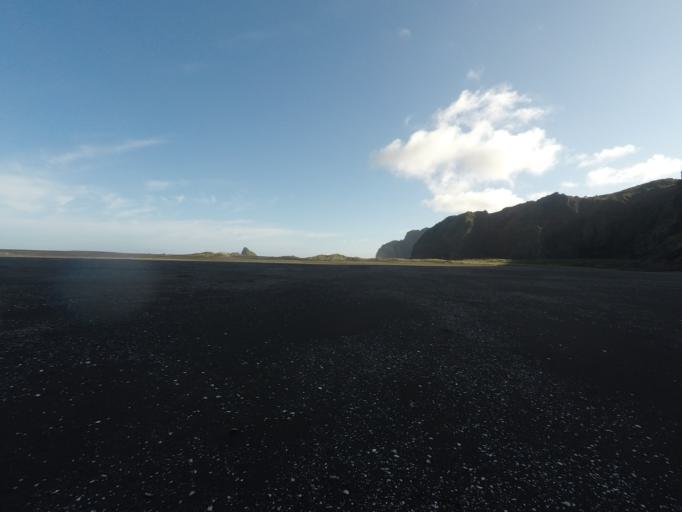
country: NZ
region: Auckland
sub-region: Auckland
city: Muriwai Beach
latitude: -36.9991
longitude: 174.4757
